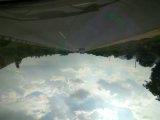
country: IN
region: Karnataka
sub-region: Kolar
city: Kolar
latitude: 13.1256
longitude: 78.0500
